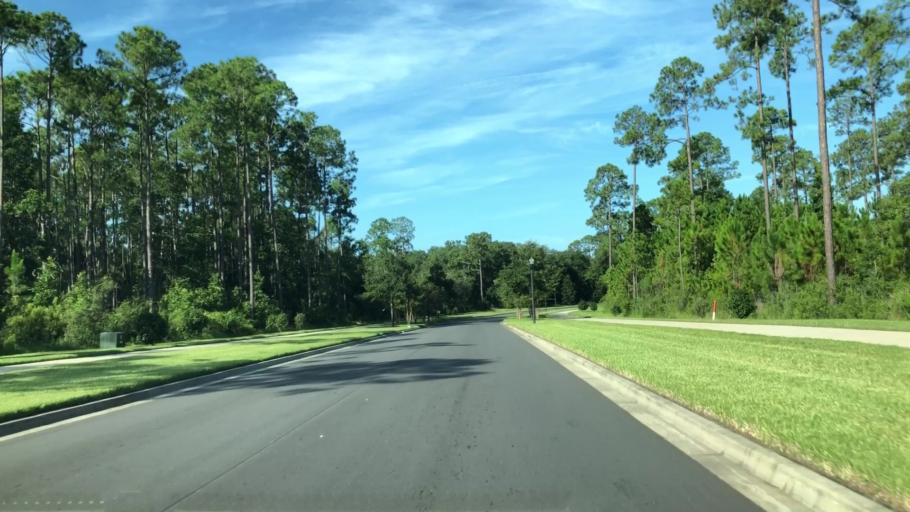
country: US
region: Florida
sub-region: Saint Johns County
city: Palm Valley
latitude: 30.1294
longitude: -81.4167
